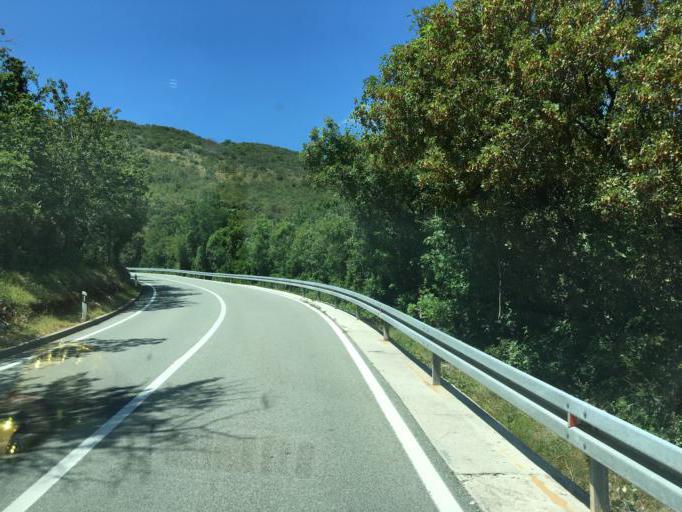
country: HR
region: Istarska
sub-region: Grad Labin
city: Rabac
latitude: 45.1530
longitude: 14.2173
